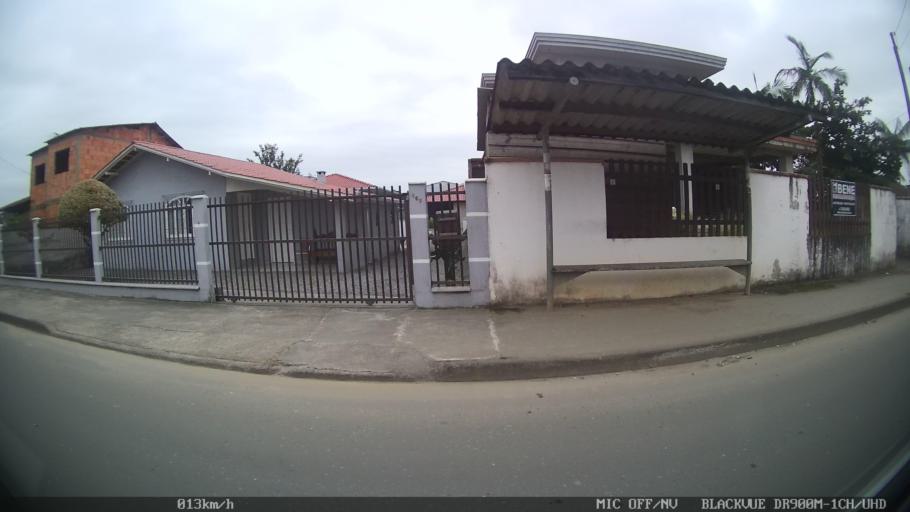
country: BR
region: Santa Catarina
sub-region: Joinville
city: Joinville
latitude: -26.3557
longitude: -48.8280
